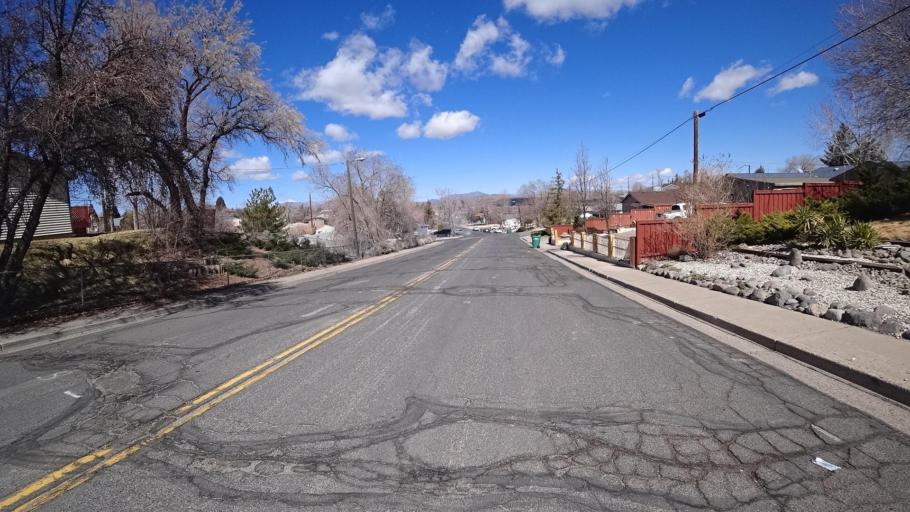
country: US
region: Nevada
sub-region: Washoe County
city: Golden Valley
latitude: 39.5895
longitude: -119.8414
